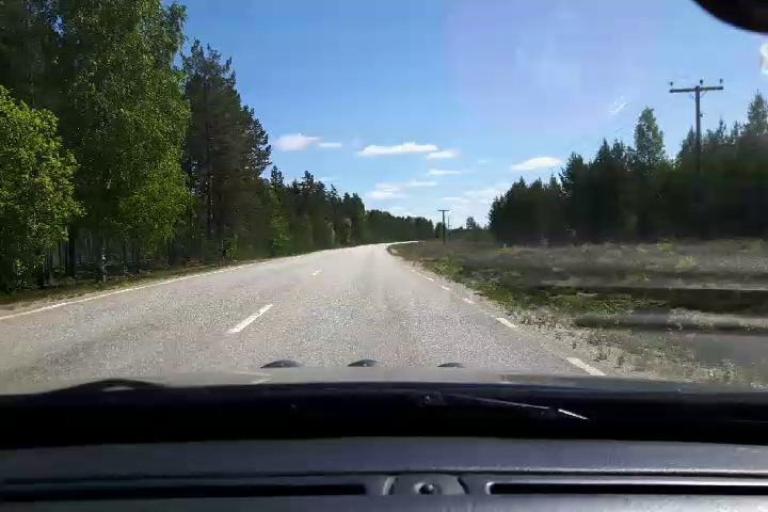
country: SE
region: Jaemtland
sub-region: Harjedalens Kommun
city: Sveg
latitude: 62.1127
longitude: 15.0552
